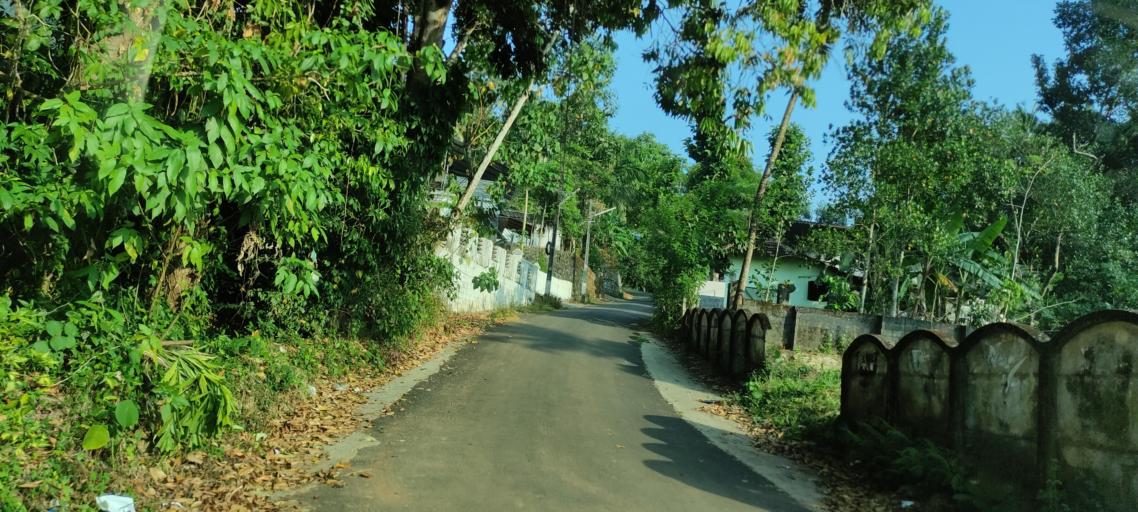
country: IN
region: Kerala
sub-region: Pattanamtitta
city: Adur
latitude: 9.1545
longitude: 76.7494
